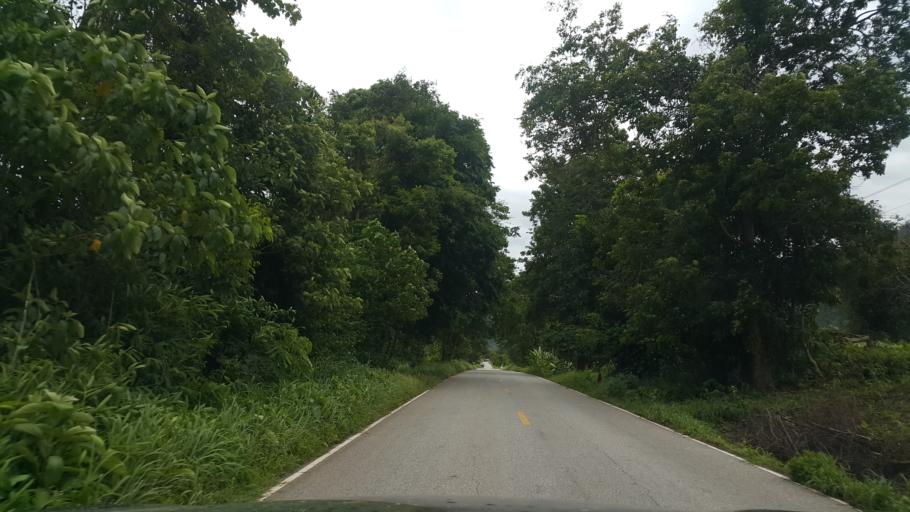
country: TH
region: Phitsanulok
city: Chat Trakan
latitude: 17.3741
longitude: 100.7448
